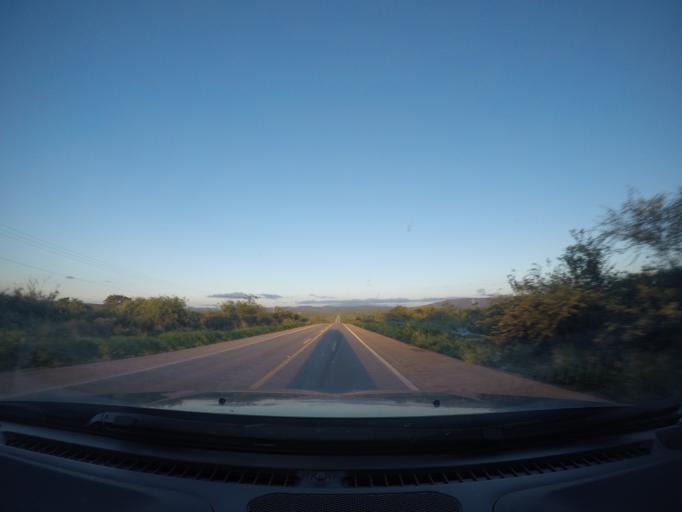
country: BR
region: Bahia
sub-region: Seabra
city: Seabra
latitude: -12.4025
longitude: -41.9492
